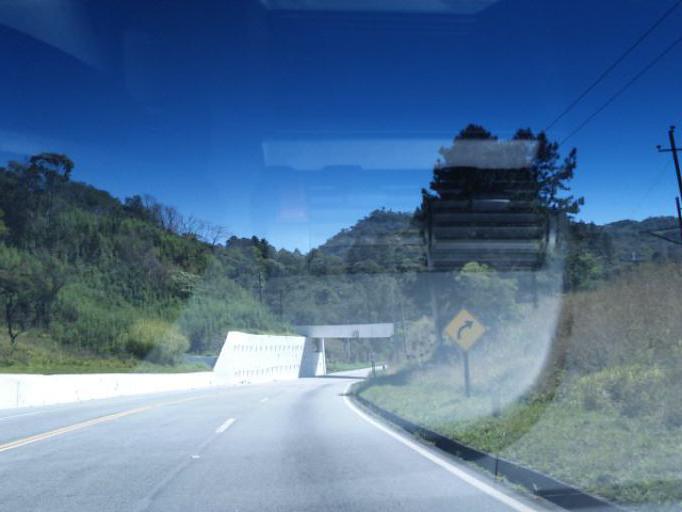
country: BR
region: Sao Paulo
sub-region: Campos Do Jordao
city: Campos do Jordao
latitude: -22.8295
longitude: -45.6261
